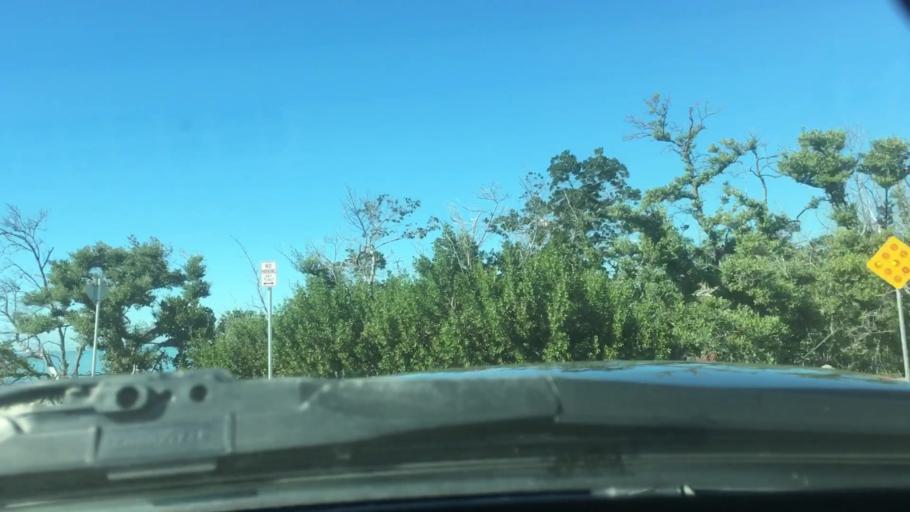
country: US
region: Florida
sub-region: Monroe County
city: Marathon
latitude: 24.7076
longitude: -81.1184
